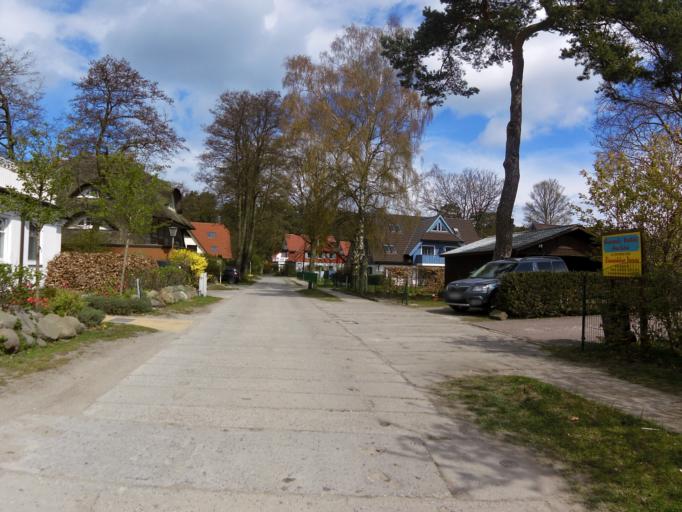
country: DE
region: Mecklenburg-Vorpommern
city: Ostseebad Prerow
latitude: 54.4483
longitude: 12.5615
